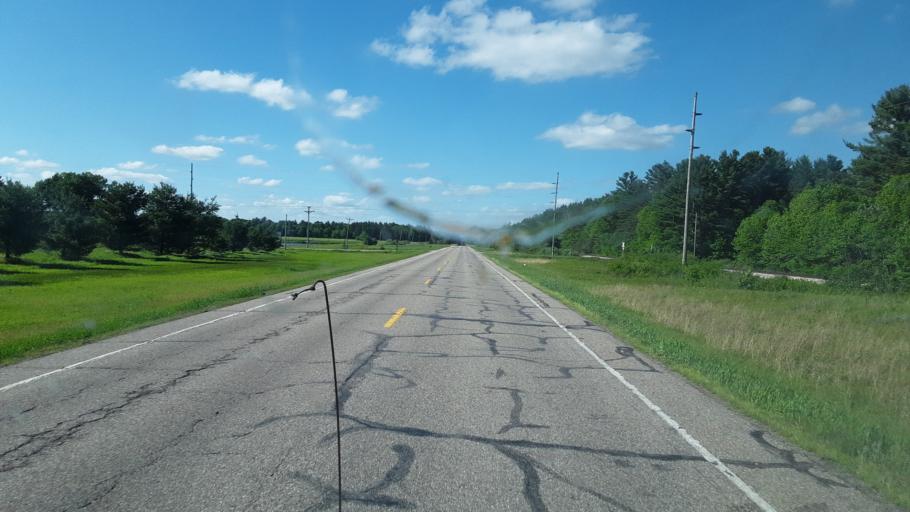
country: US
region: Wisconsin
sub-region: Wood County
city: Nekoosa
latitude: 44.2407
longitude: -90.1392
